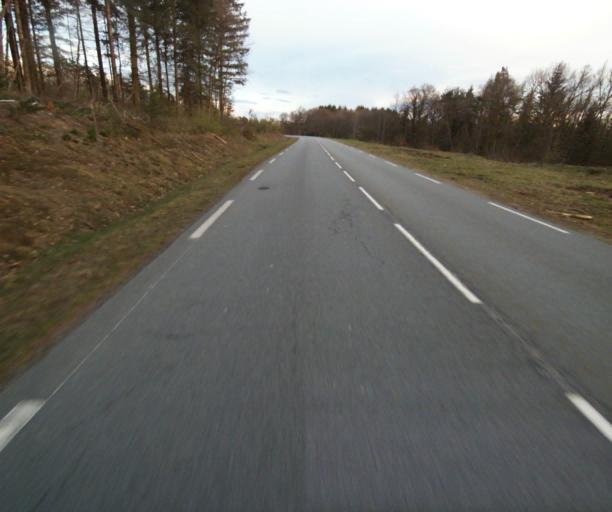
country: FR
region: Limousin
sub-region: Departement de la Correze
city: Correze
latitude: 45.2871
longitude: 1.9043
